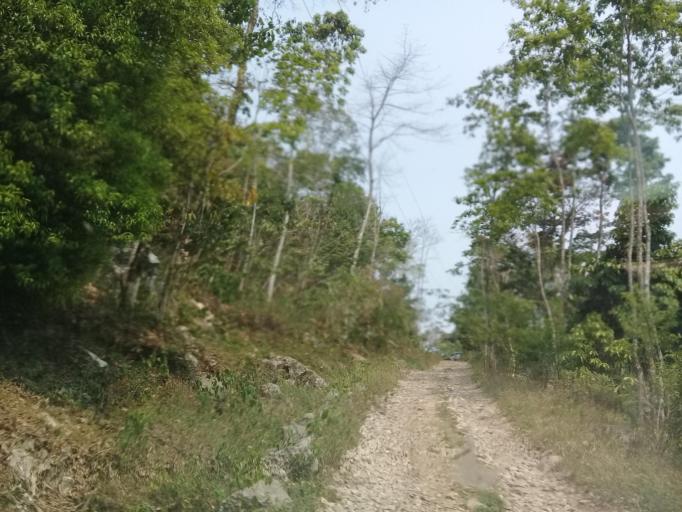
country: MX
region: Veracruz
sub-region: Tezonapa
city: Laguna Chica (Pueblo Nuevo)
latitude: 18.5828
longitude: -96.7553
